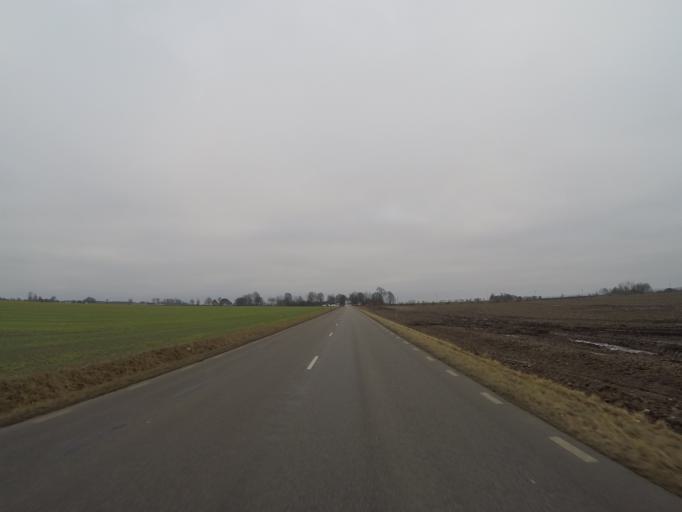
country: SE
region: Skane
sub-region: Hoors Kommun
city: Loberod
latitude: 55.7808
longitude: 13.4218
